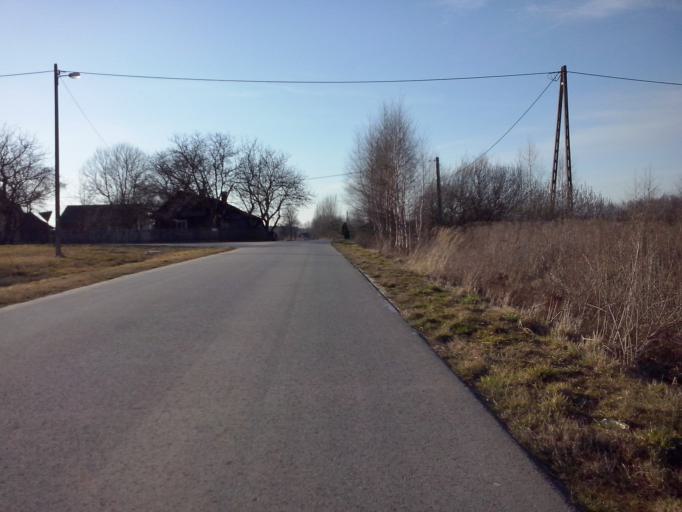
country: PL
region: Subcarpathian Voivodeship
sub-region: Powiat nizanski
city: Krzeszow
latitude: 50.4111
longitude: 22.3567
